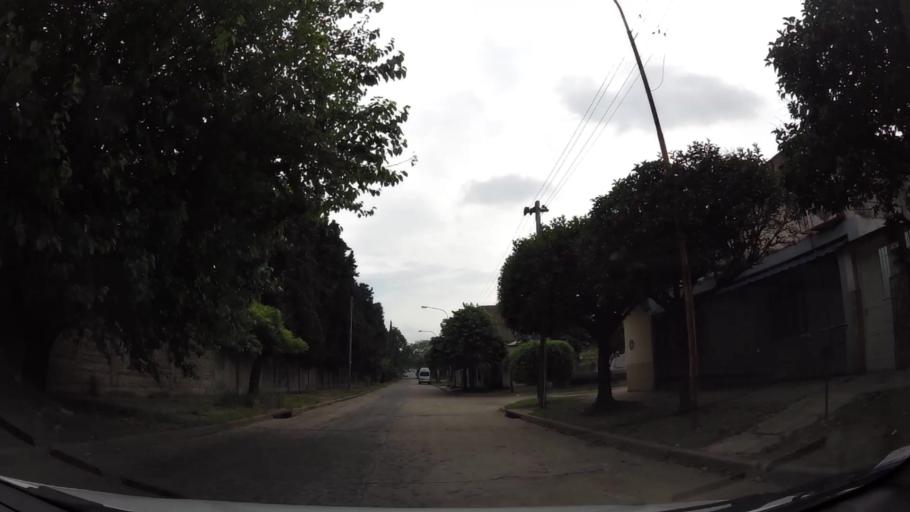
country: AR
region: Buenos Aires
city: San Justo
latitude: -34.6928
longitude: -58.5188
